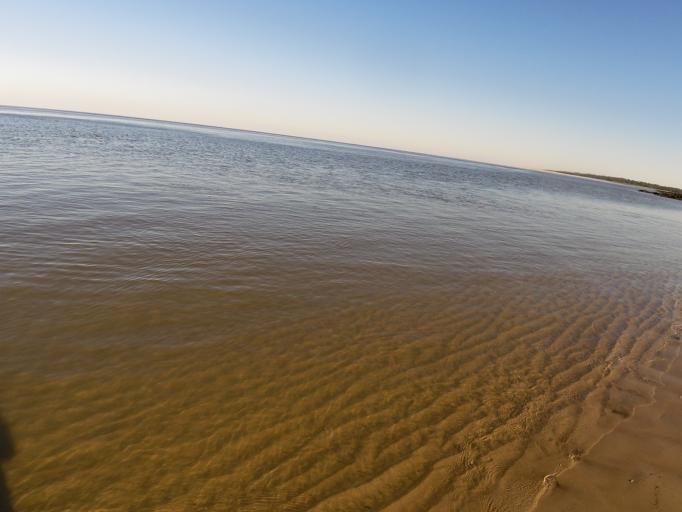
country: US
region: Florida
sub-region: Duval County
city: Atlantic Beach
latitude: 30.4971
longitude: -81.4410
